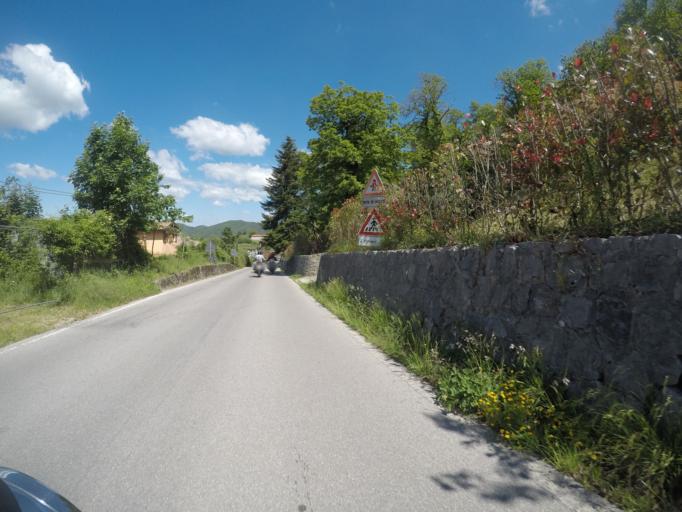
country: IT
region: Tuscany
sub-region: Provincia di Lucca
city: Careggine
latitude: 44.1169
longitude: 10.3296
